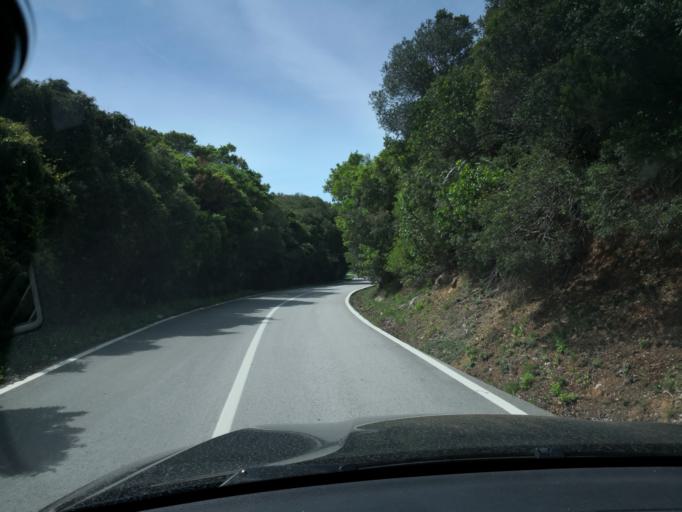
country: PT
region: Setubal
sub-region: Sesimbra
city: Sesimbra
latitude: 38.4648
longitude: -8.9997
